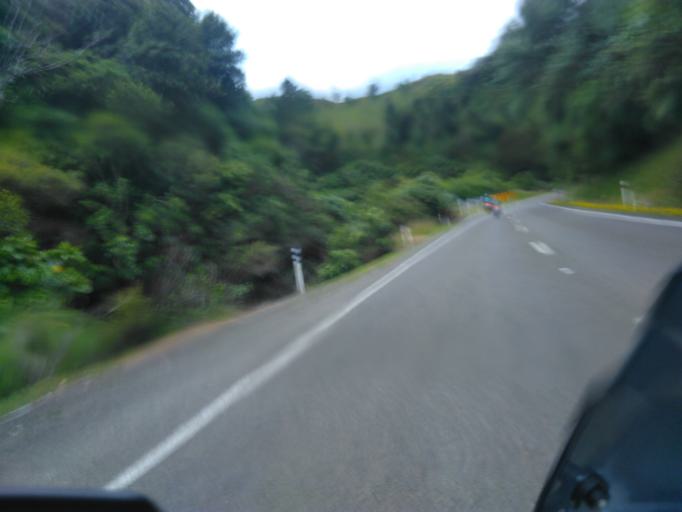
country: NZ
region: Bay of Plenty
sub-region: Opotiki District
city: Opotiki
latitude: -38.3397
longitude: 177.4349
